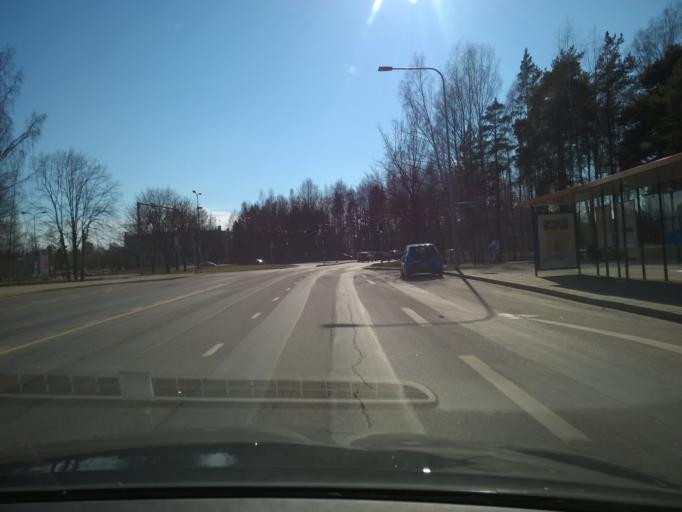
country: FI
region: Uusimaa
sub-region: Helsinki
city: Teekkarikylae
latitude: 60.2146
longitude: 24.8866
